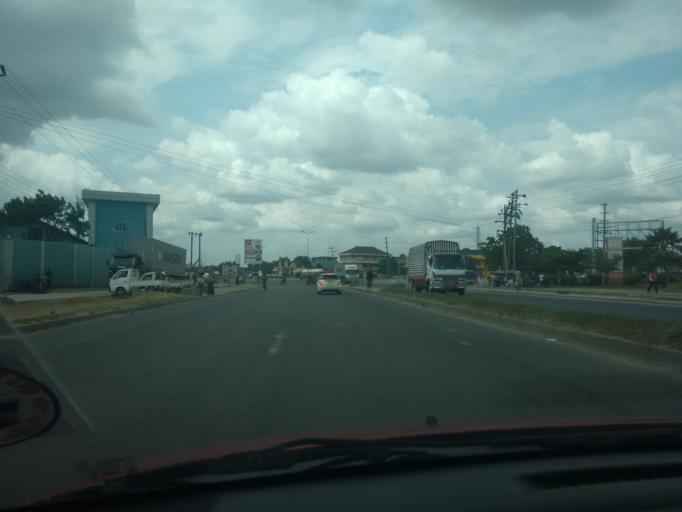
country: TZ
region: Dar es Salaam
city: Dar es Salaam
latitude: -6.8488
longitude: 39.2503
